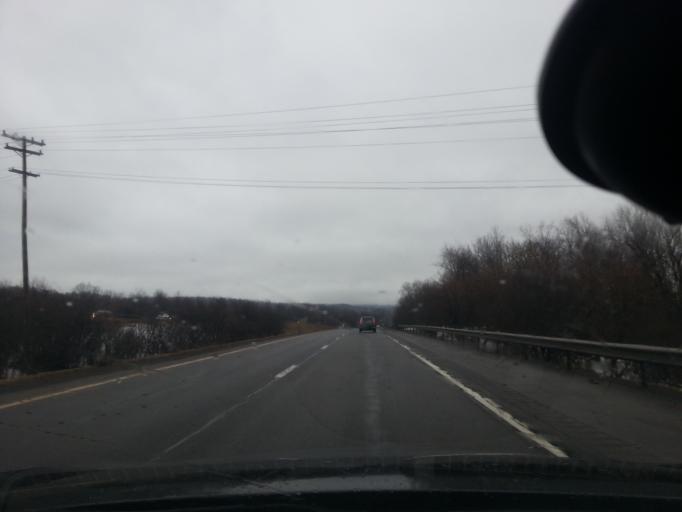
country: US
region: New York
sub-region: Onondaga County
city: Nedrow
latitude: 42.9841
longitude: -76.1327
